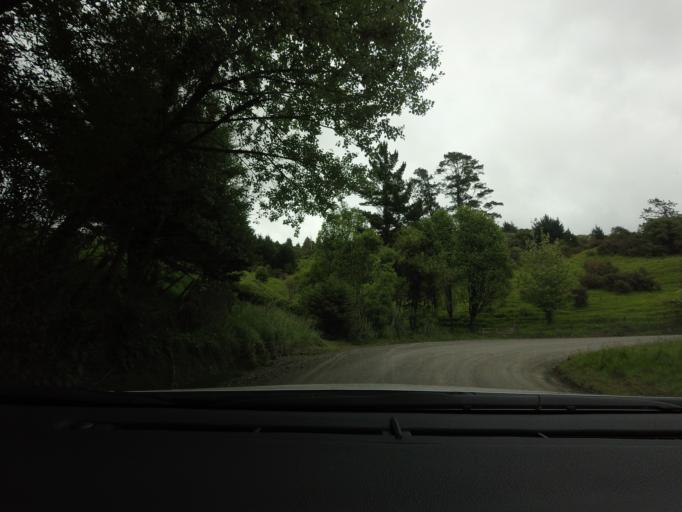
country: NZ
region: Auckland
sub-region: Auckland
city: Warkworth
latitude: -36.4890
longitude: 174.6179
